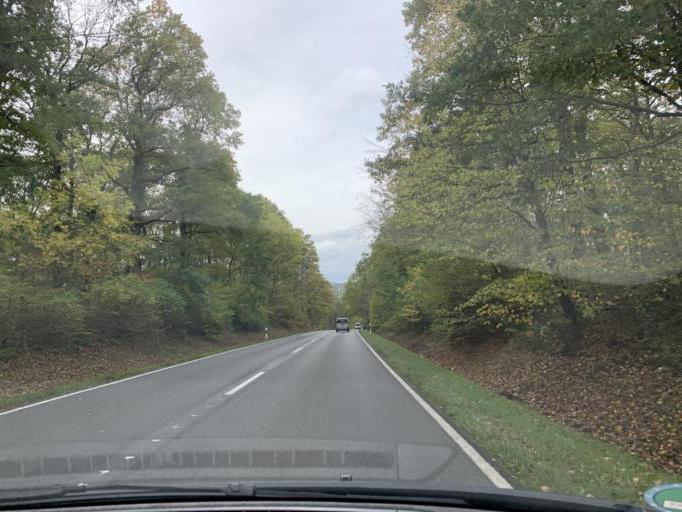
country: DE
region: North Rhine-Westphalia
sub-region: Regierungsbezirk Koln
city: Kreuzau
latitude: 50.7392
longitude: 6.5133
